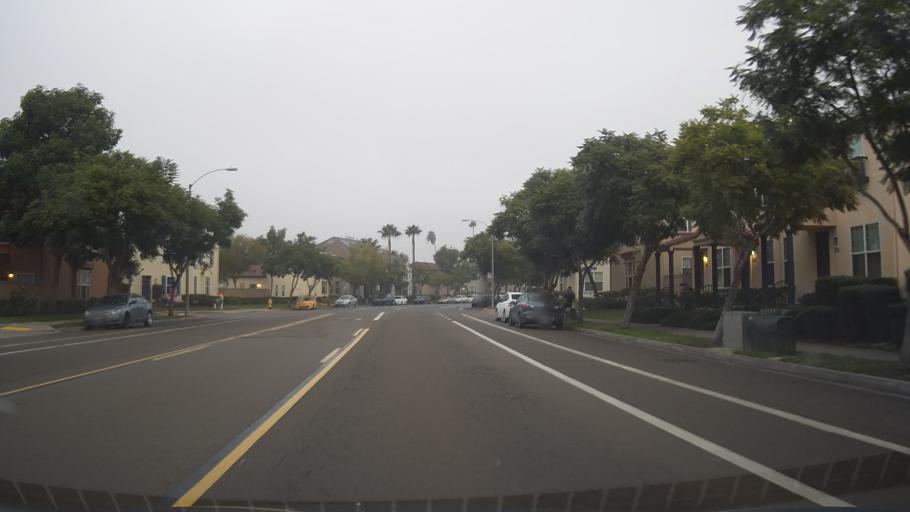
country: US
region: California
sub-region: San Diego County
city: San Diego
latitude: 32.8025
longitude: -117.1413
